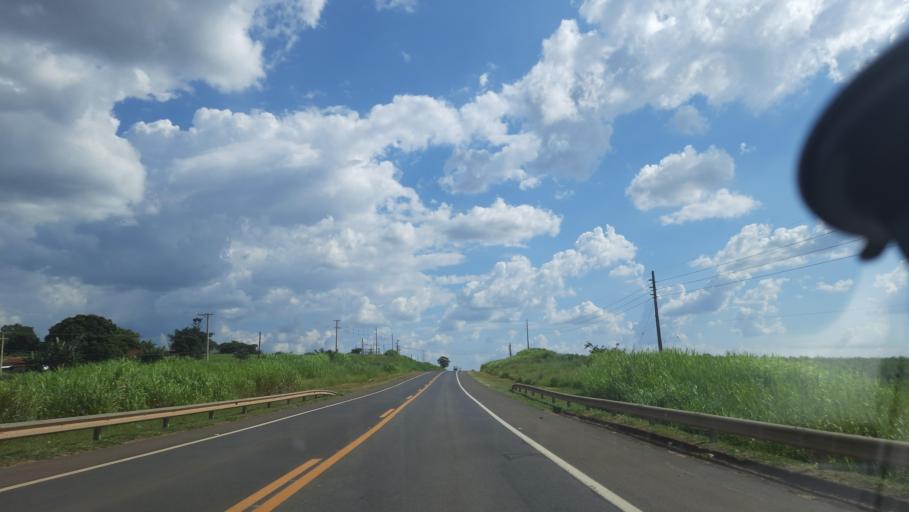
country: BR
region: Sao Paulo
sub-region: Sao Jose Do Rio Pardo
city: Sao Jose do Rio Pardo
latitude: -21.6795
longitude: -46.9267
